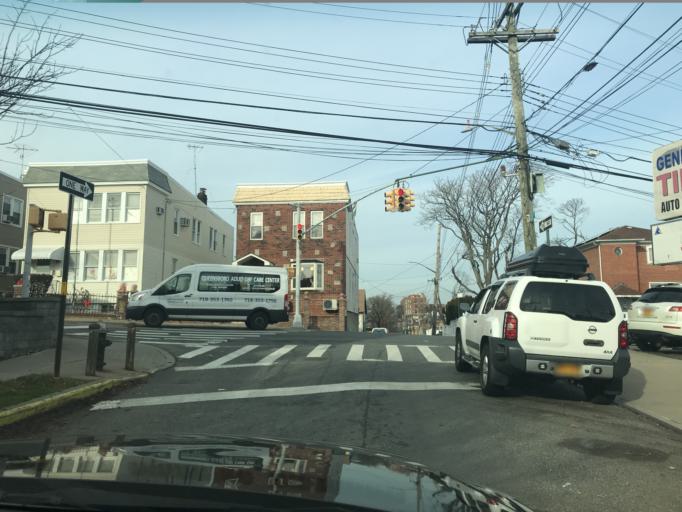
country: US
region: New York
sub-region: Bronx
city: The Bronx
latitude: 40.7847
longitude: -73.8403
